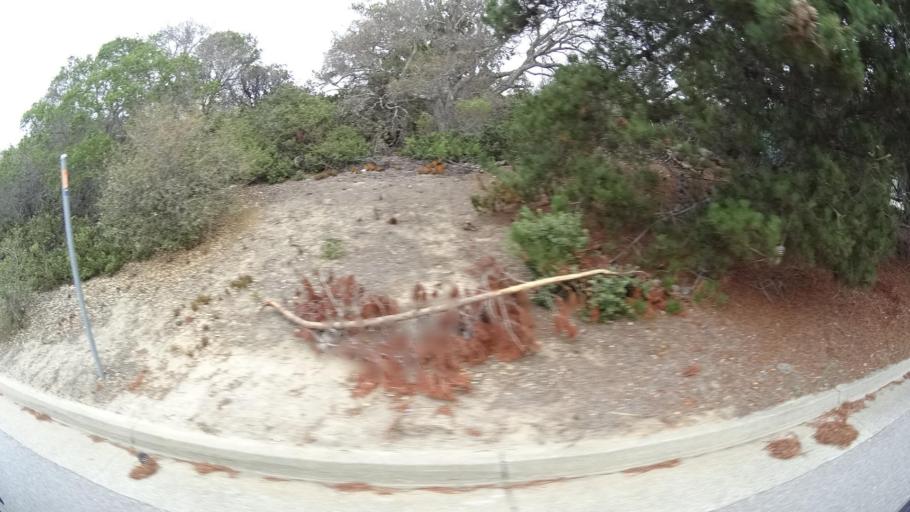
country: US
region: California
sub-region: Monterey County
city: Del Rey Oaks
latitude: 36.5771
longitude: -121.8108
